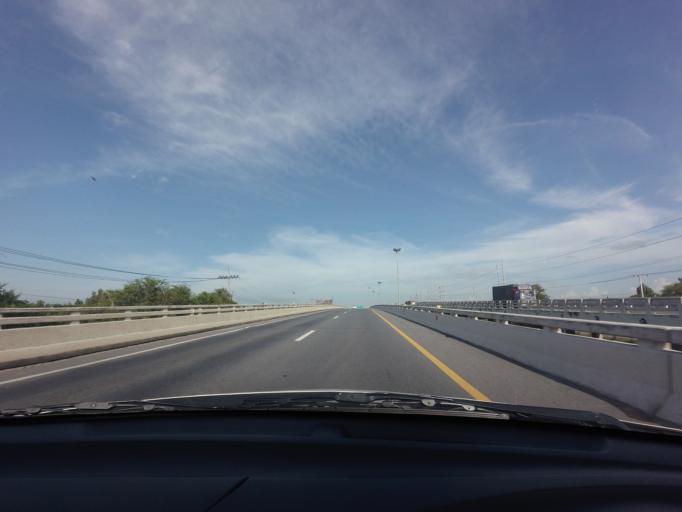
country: TH
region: Suphan Buri
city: Bang Pla Ma
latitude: 14.3286
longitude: 100.2136
